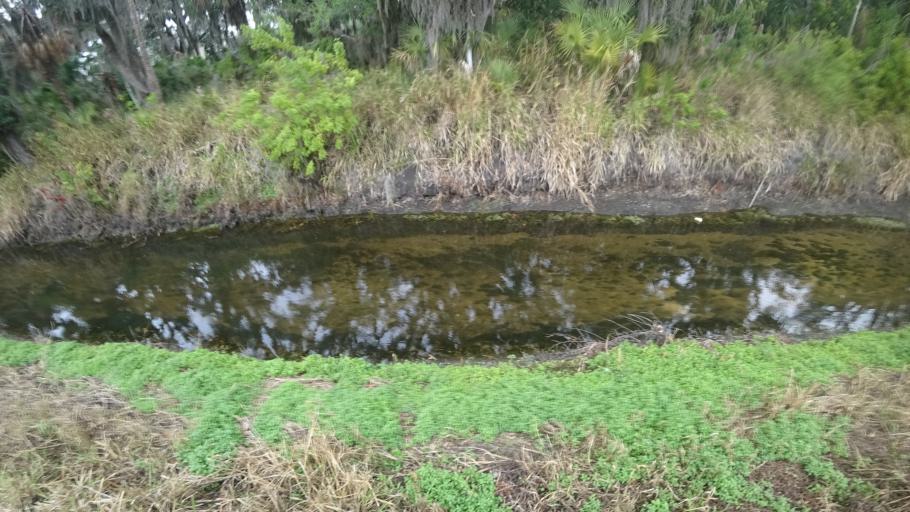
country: US
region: Florida
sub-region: Manatee County
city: Ellenton
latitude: 27.5913
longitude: -82.4888
